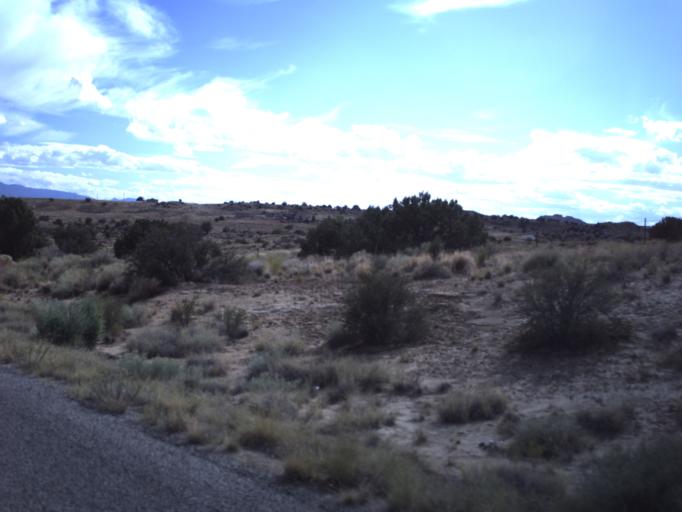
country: US
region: Colorado
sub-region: Montezuma County
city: Towaoc
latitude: 37.1860
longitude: -109.1269
